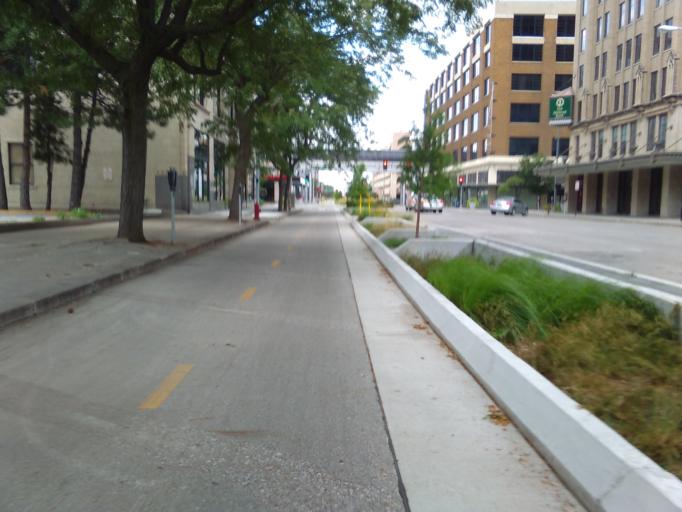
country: US
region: Nebraska
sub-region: Lancaster County
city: Lincoln
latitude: 40.8125
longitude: -96.7017
